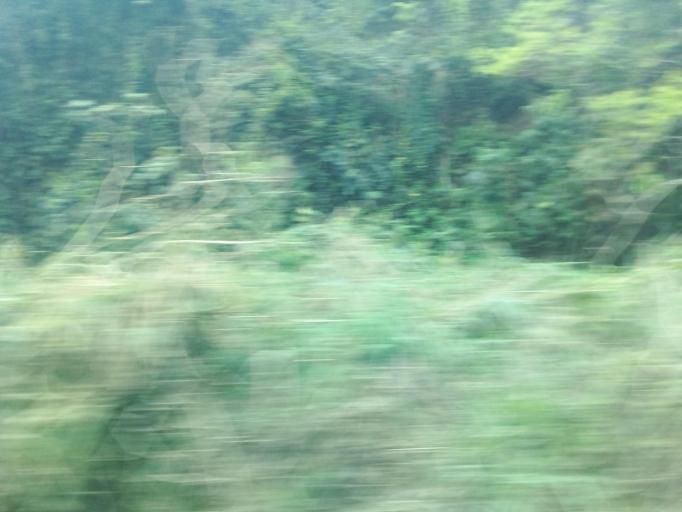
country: BR
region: Minas Gerais
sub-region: Ipaba
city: Ipaba
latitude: -19.4631
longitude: -42.4578
